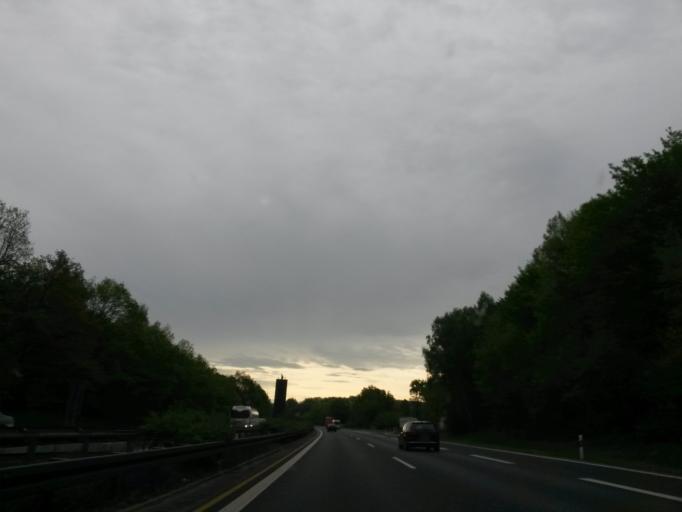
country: DE
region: Bavaria
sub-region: Regierungsbezirk Unterfranken
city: Wiesenbronn
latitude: 49.7743
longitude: 10.3176
